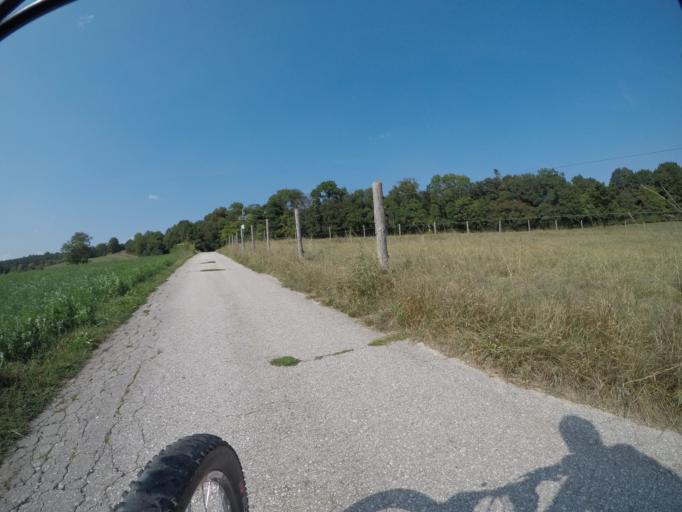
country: AT
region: Lower Austria
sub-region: Politischer Bezirk Baden
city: Berndorf
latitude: 47.9538
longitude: 16.1114
